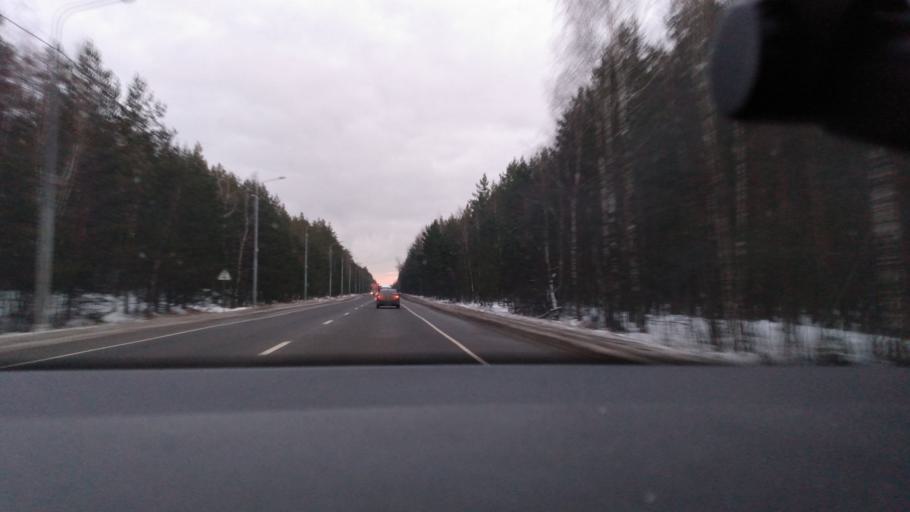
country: RU
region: Moskovskaya
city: Il'inskiy Pogost
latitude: 55.4705
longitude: 38.9622
